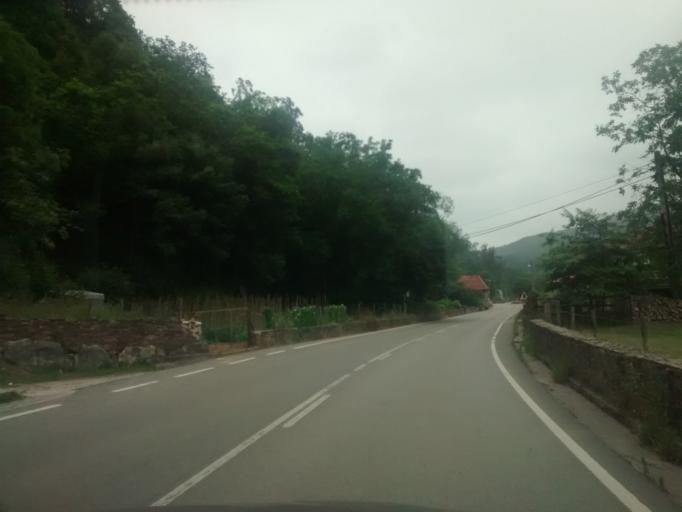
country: ES
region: Cantabria
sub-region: Provincia de Cantabria
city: Ruente
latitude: 43.2321
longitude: -4.2966
